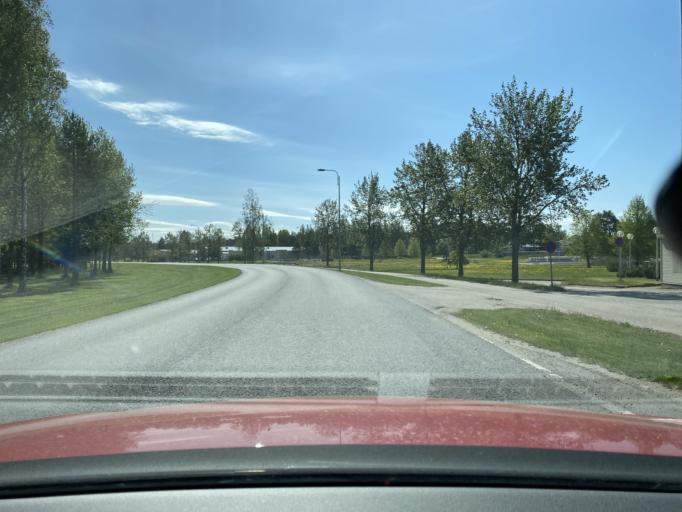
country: FI
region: Satakunta
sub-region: Rauma
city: Eura
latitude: 61.1270
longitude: 22.1463
